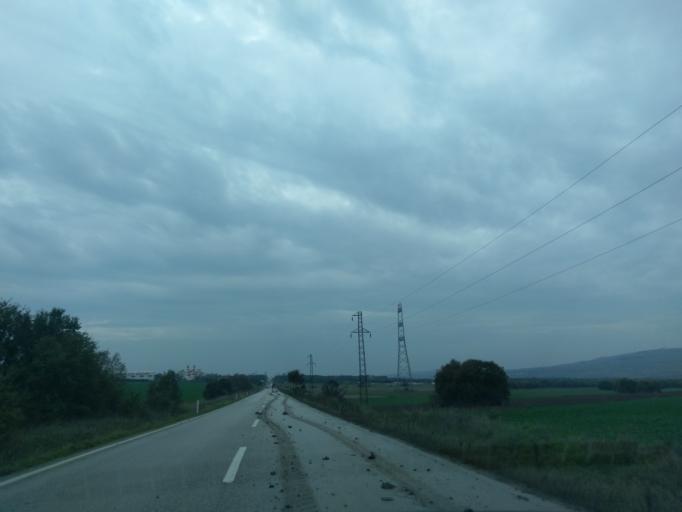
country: TR
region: Istanbul
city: Canta
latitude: 41.1499
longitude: 28.1068
